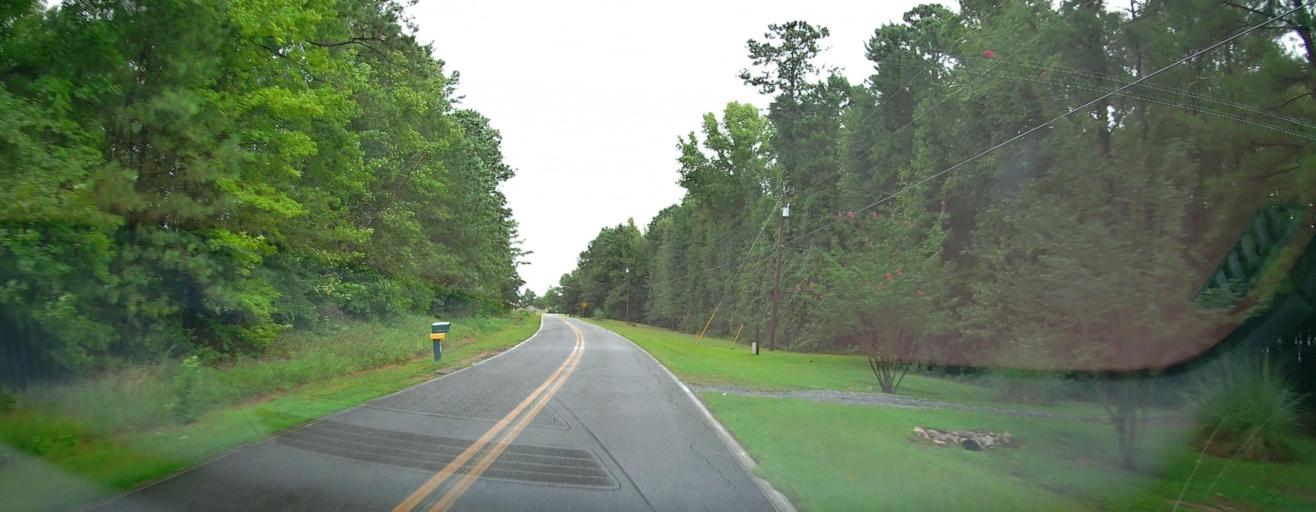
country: US
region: Georgia
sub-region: Bibb County
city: West Point
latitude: 32.8047
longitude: -83.8258
